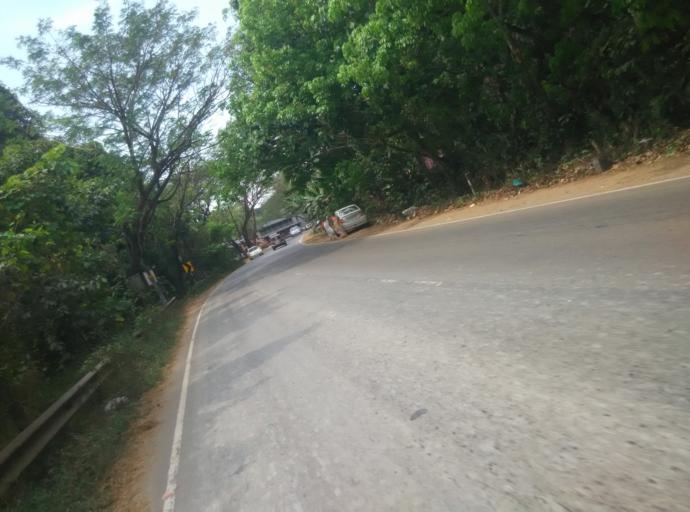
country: IN
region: Kerala
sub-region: Kottayam
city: Lalam
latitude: 9.6997
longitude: 76.6537
